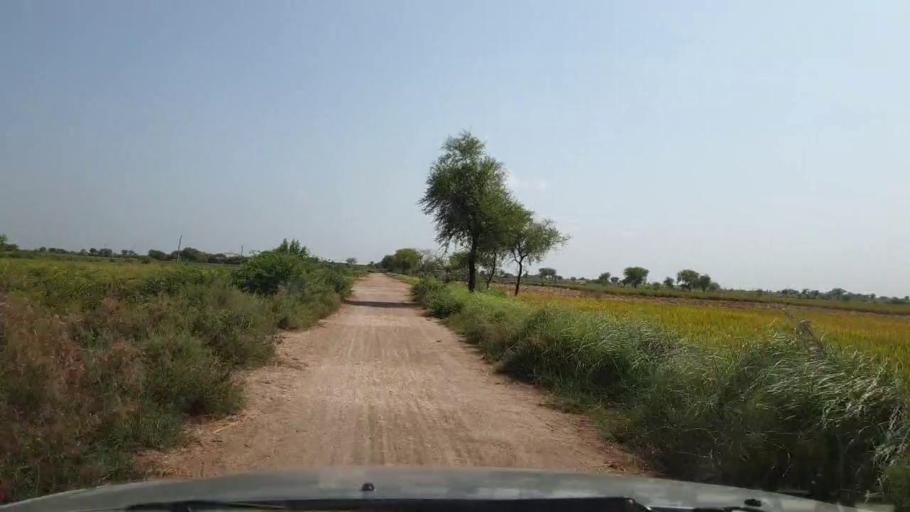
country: PK
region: Sindh
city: Rajo Khanani
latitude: 25.0207
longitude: 68.7983
